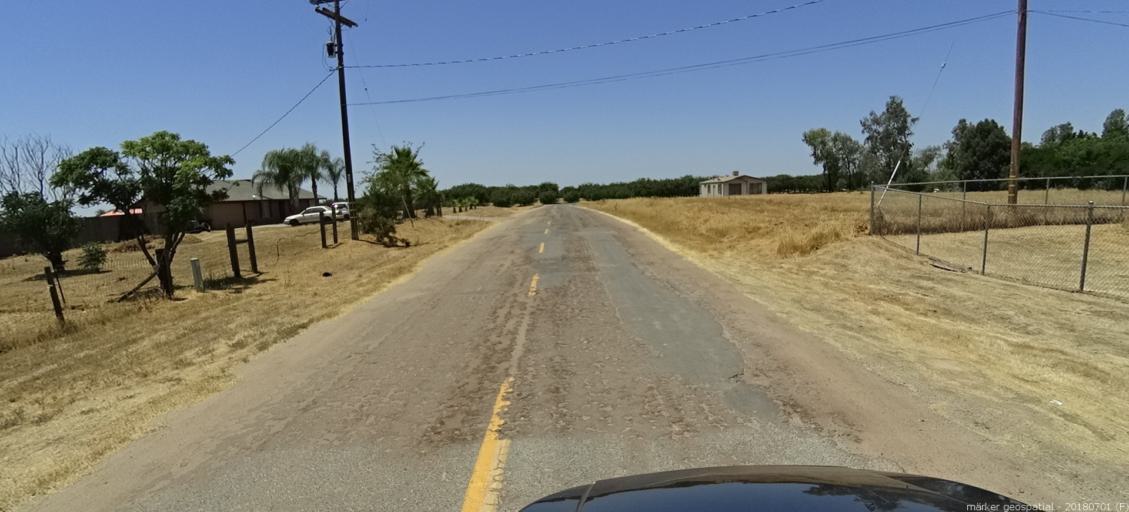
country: US
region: California
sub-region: Madera County
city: Madera Acres
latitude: 37.0336
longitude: -119.9999
